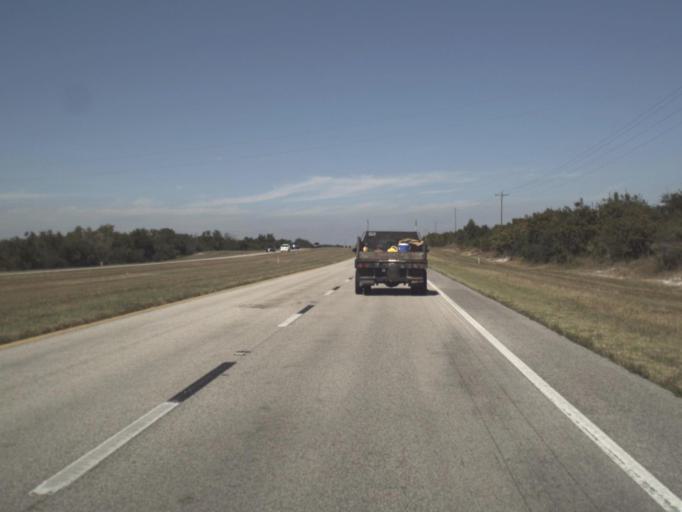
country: US
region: Florida
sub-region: Highlands County
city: Placid Lakes
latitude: 27.1287
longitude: -81.3298
